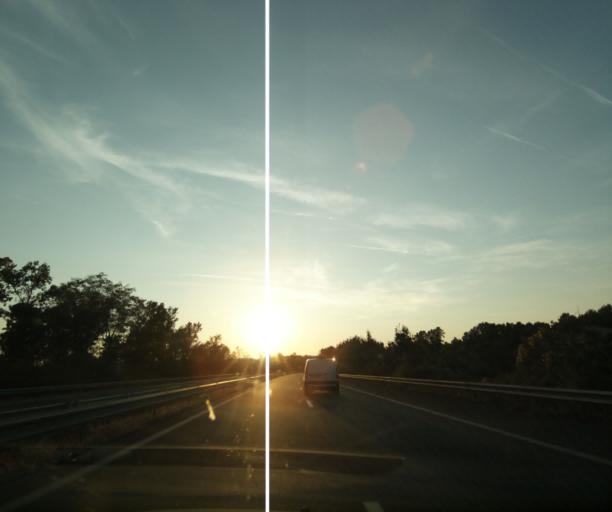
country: FR
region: Aquitaine
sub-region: Departement du Lot-et-Garonne
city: Vianne
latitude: 44.2287
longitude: 0.3413
